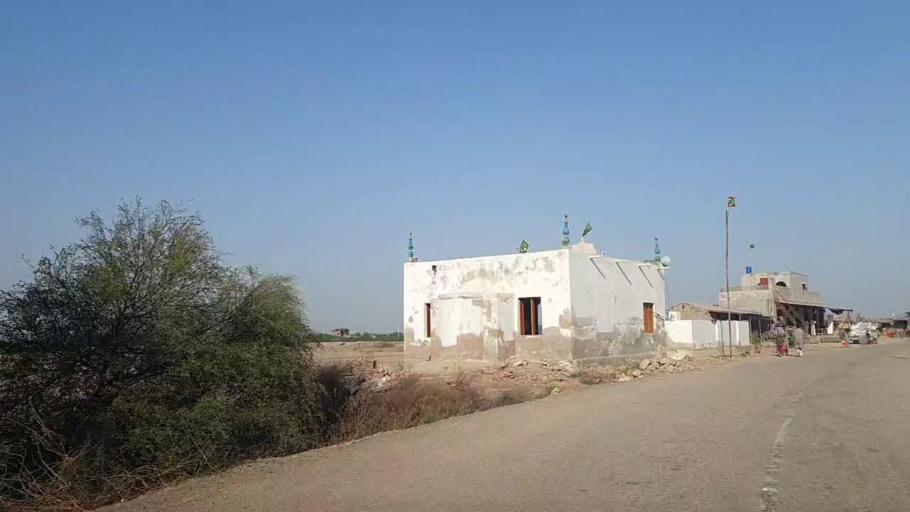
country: PK
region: Sindh
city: Mirpur Batoro
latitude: 24.5800
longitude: 68.3945
